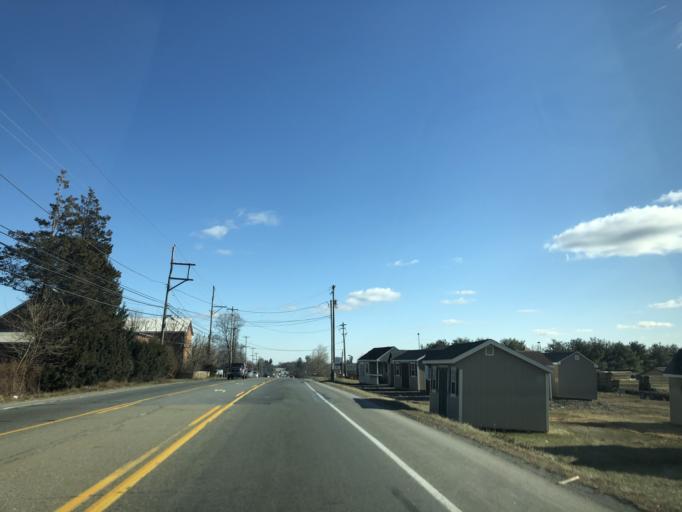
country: US
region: Pennsylvania
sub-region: Chester County
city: Parkesburg
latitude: 39.9841
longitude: -75.9385
